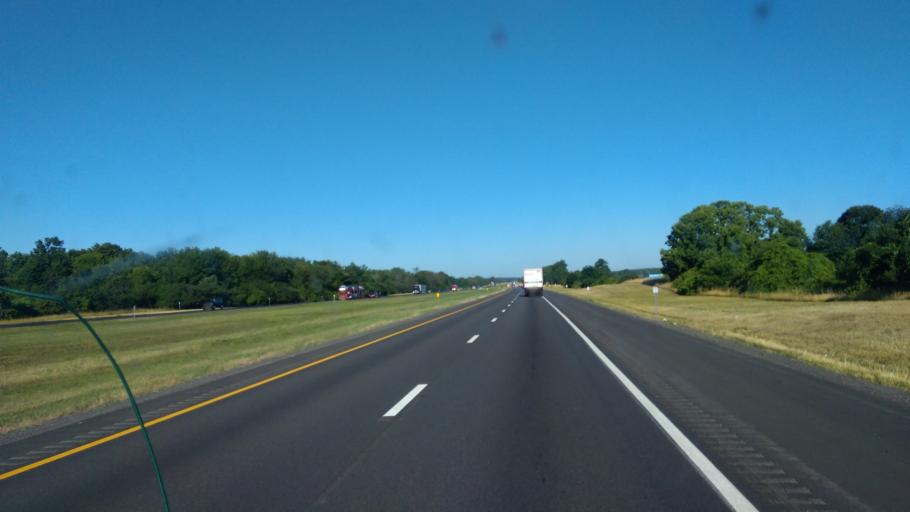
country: US
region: New York
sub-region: Ontario County
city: Clifton Springs
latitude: 42.9746
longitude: -77.1038
